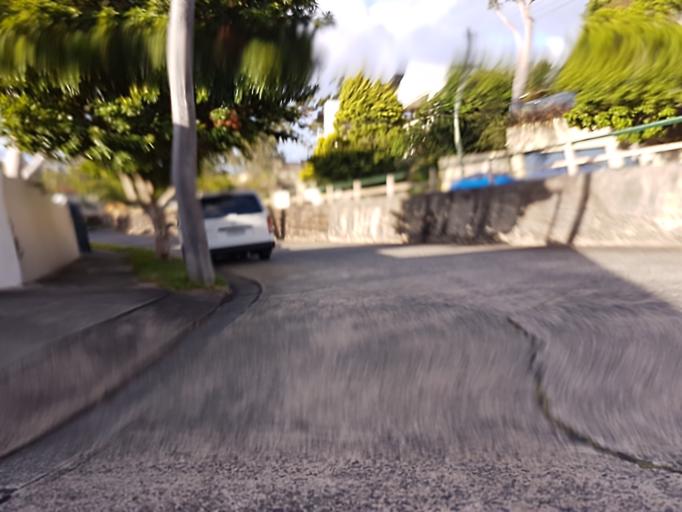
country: AU
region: New South Wales
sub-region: Willoughby
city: Castlecrag
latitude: -33.8111
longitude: 151.2371
